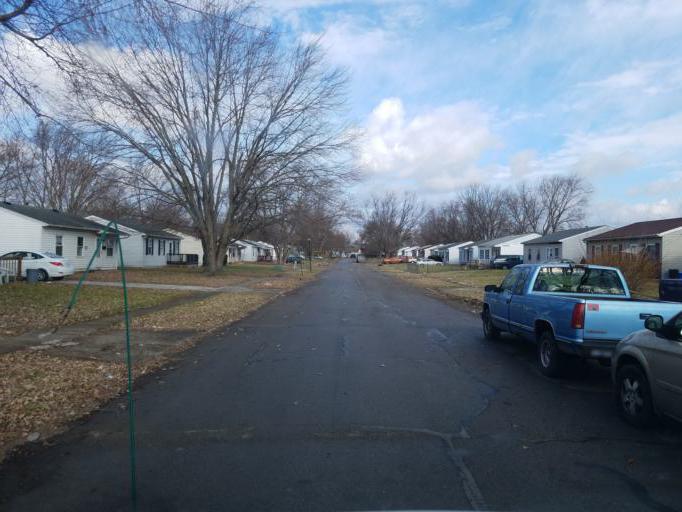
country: US
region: Ohio
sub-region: Marion County
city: Marion
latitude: 40.5798
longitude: -83.1517
